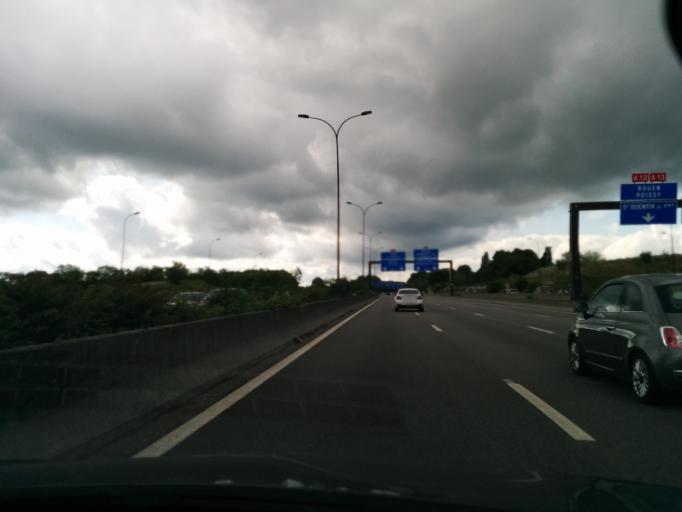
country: FR
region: Ile-de-France
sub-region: Departement des Yvelines
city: Rocquencourt
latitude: 48.8407
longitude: 2.1106
